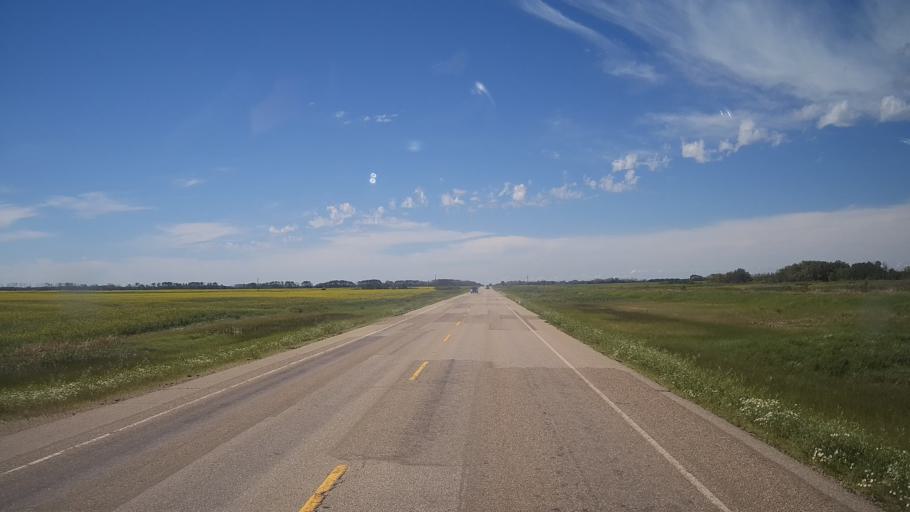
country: CA
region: Saskatchewan
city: Langenburg
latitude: 50.7828
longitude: -101.5252
